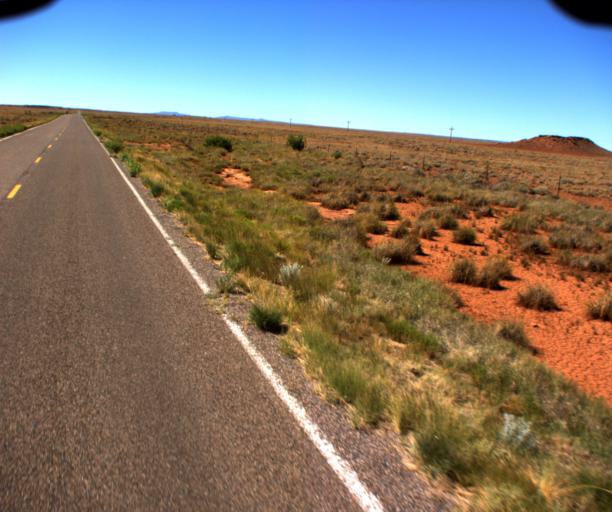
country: US
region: Arizona
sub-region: Coconino County
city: LeChee
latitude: 35.2253
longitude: -110.9546
